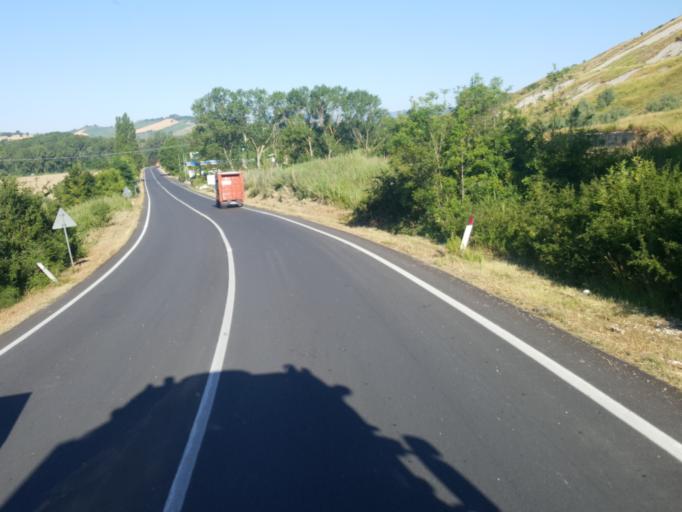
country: IT
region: The Marches
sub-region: Provincia di Pesaro e Urbino
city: Montecalvo in Foglia
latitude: 43.7914
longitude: 12.6381
